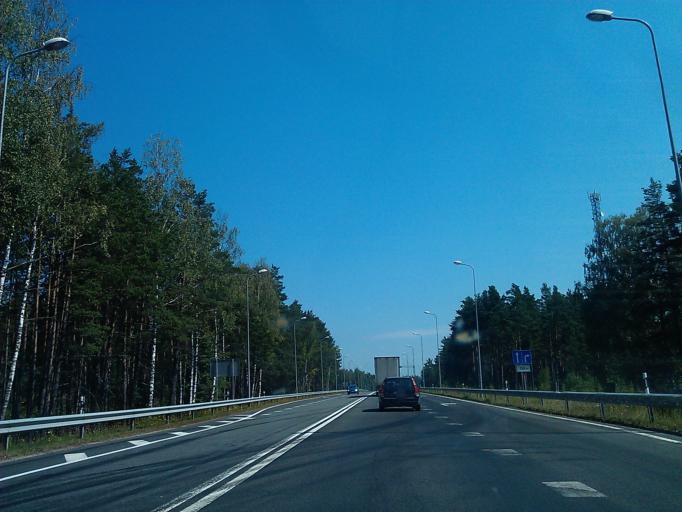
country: LV
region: Saulkrastu
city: Saulkrasti
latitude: 57.1913
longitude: 24.3515
